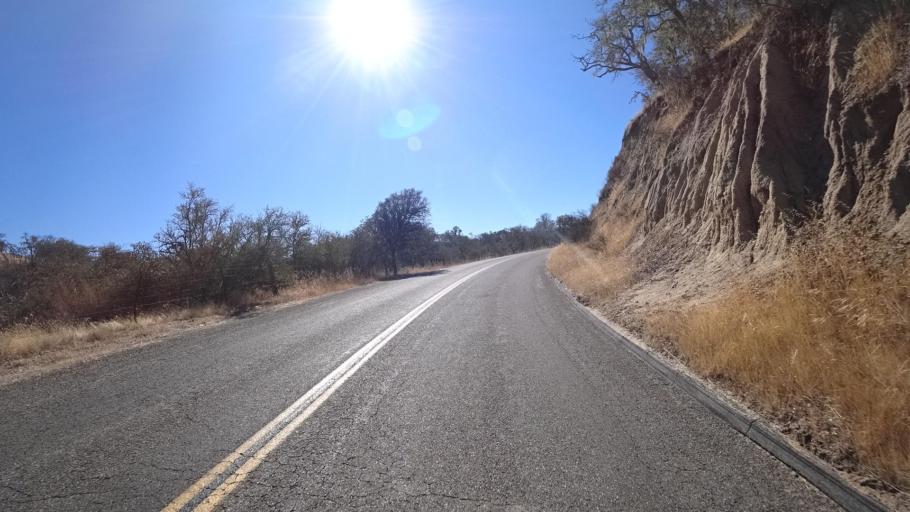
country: US
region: California
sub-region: Monterey County
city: Gonzales
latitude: 36.4041
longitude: -121.5874
